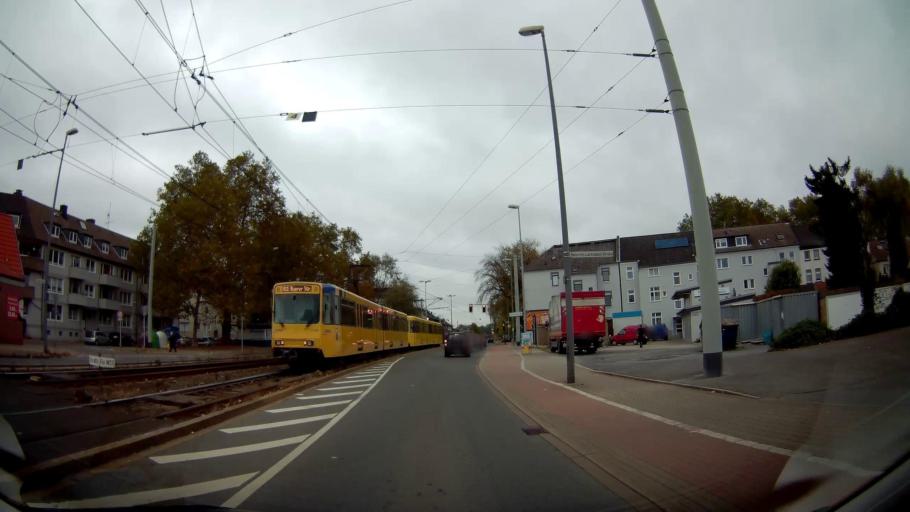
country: DE
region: North Rhine-Westphalia
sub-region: Regierungsbezirk Munster
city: Gladbeck
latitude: 51.5334
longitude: 7.0152
